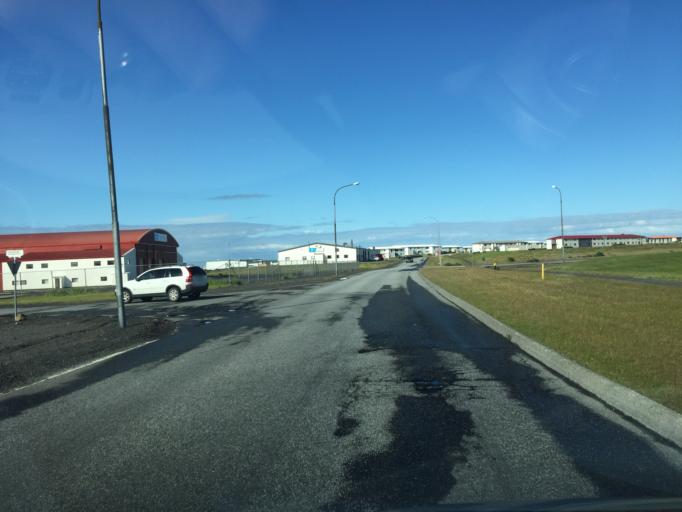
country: IS
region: Southern Peninsula
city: Reykjanesbaer
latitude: 63.9681
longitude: -22.5762
